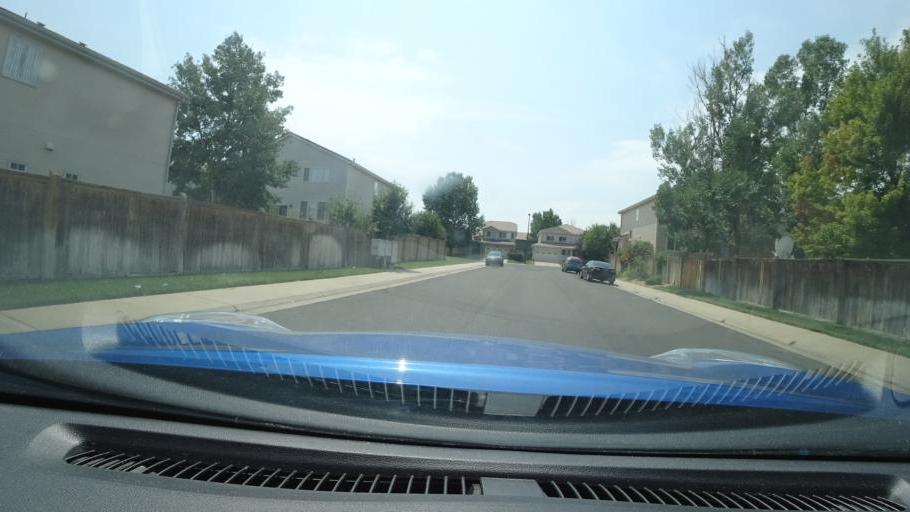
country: US
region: Colorado
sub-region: Adams County
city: Aurora
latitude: 39.7720
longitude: -104.7546
